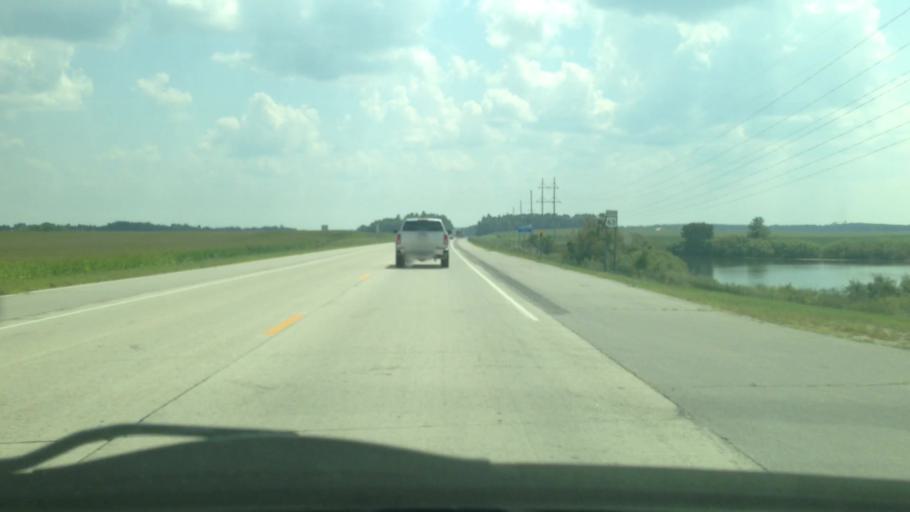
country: US
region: Minnesota
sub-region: Fillmore County
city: Spring Valley
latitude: 43.6455
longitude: -92.3894
